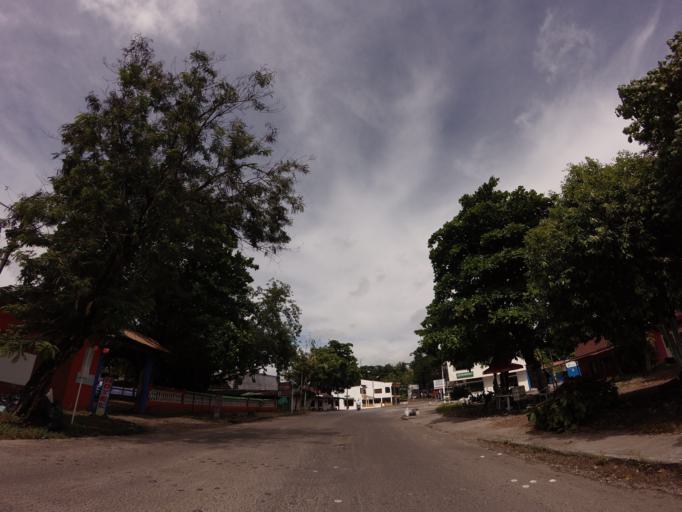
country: CO
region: Caldas
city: La Dorada
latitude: 5.4470
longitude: -74.6696
